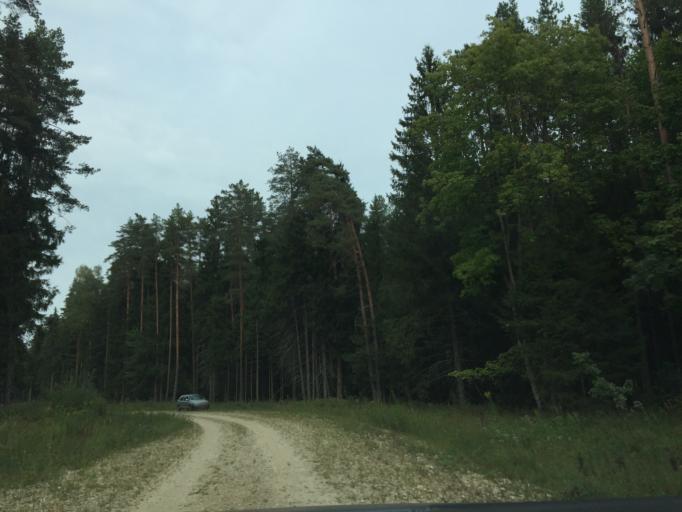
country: LV
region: Baldone
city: Baldone
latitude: 56.7501
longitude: 24.4664
